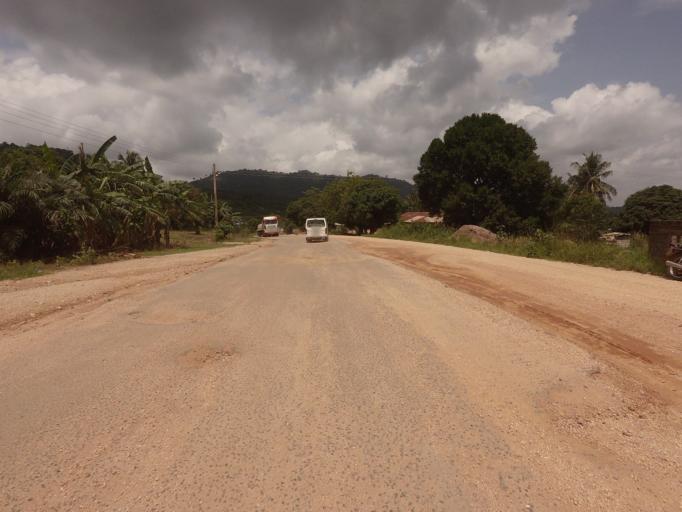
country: GH
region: Volta
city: Ho
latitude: 6.6966
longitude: 0.3351
